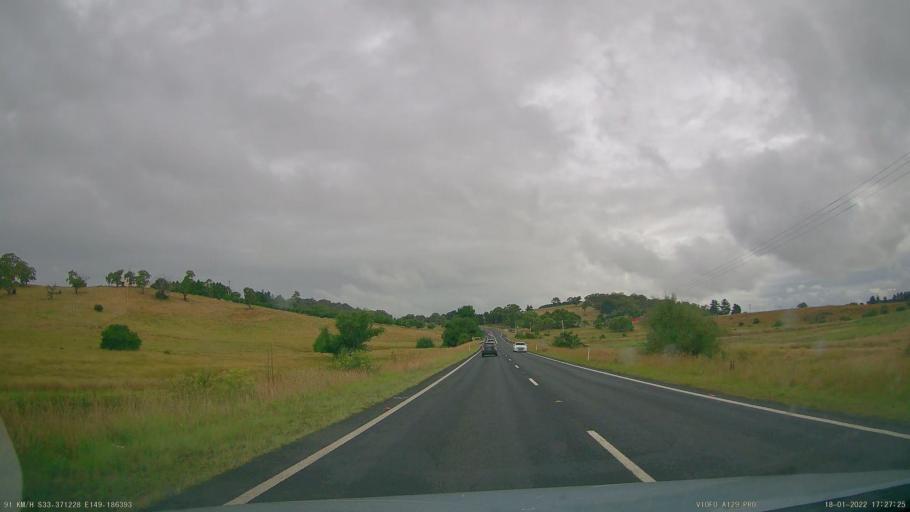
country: AU
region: New South Wales
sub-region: Blayney
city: Millthorpe
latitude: -33.3715
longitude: 149.1866
